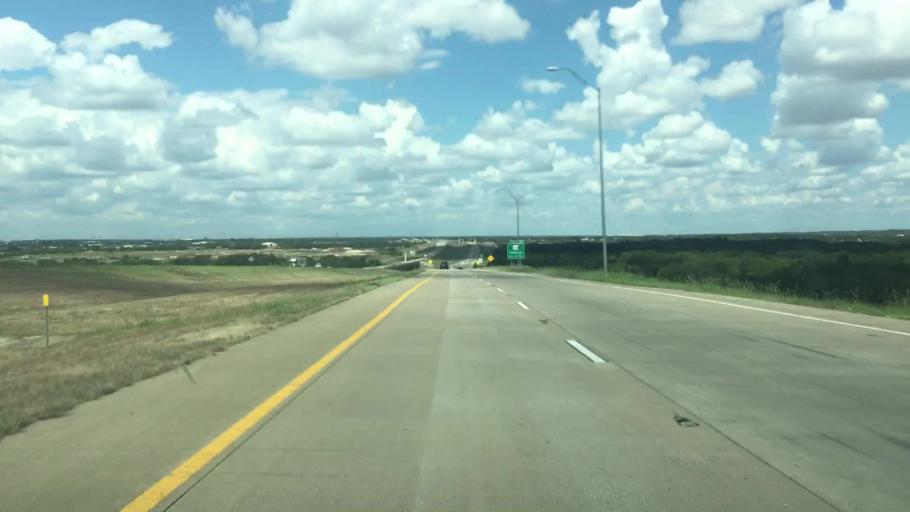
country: US
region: Texas
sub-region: Williamson County
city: Georgetown
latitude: 30.6490
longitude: -97.6332
